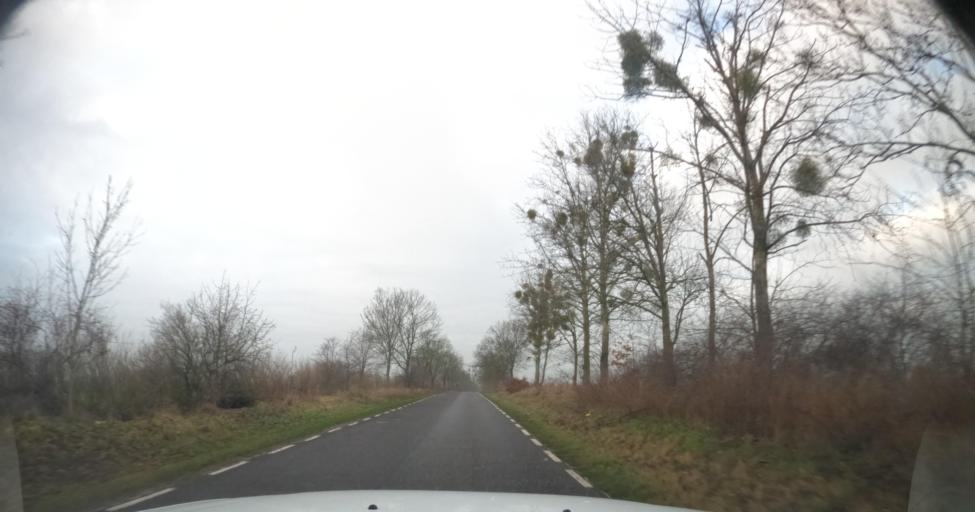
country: PL
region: West Pomeranian Voivodeship
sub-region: Powiat mysliborski
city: Boleszkowice
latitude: 52.7385
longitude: 14.6238
